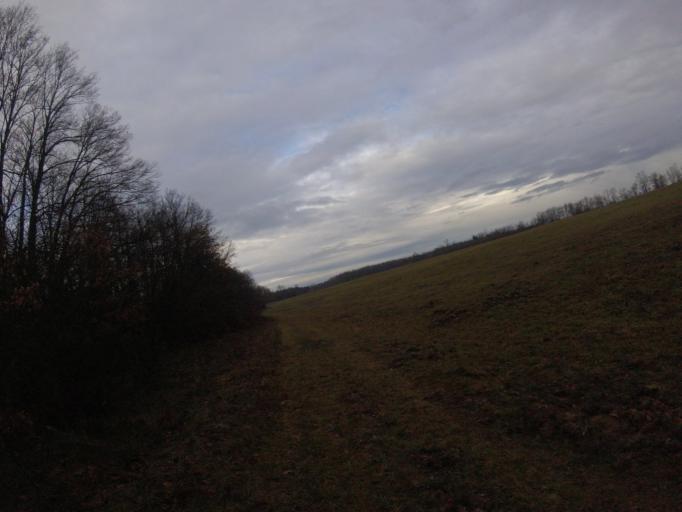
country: HU
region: Vas
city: Sarvar
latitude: 47.2393
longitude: 17.0061
